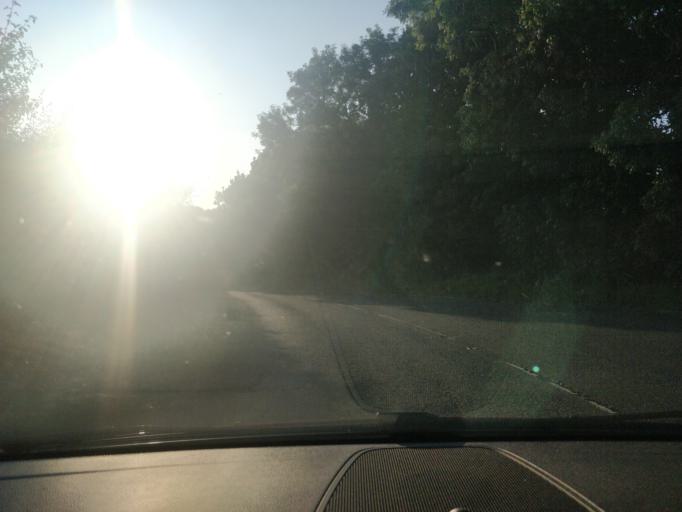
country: GB
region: England
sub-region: Lancashire
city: Parbold
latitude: 53.6066
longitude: -2.7765
